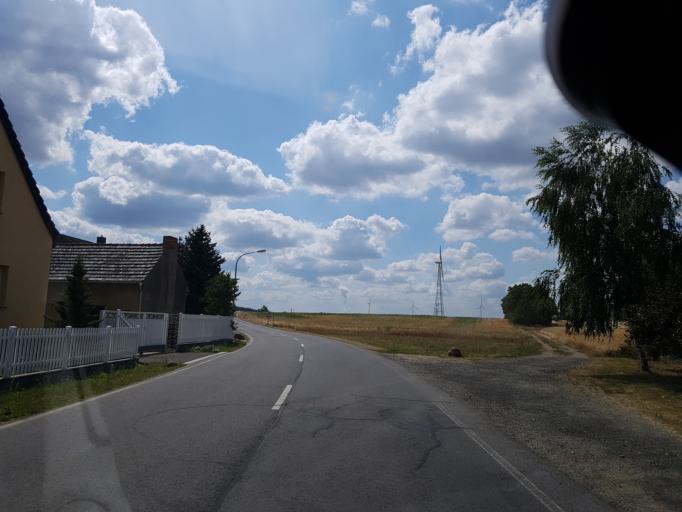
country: DE
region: Brandenburg
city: Drebkau
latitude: 51.6830
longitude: 14.2760
